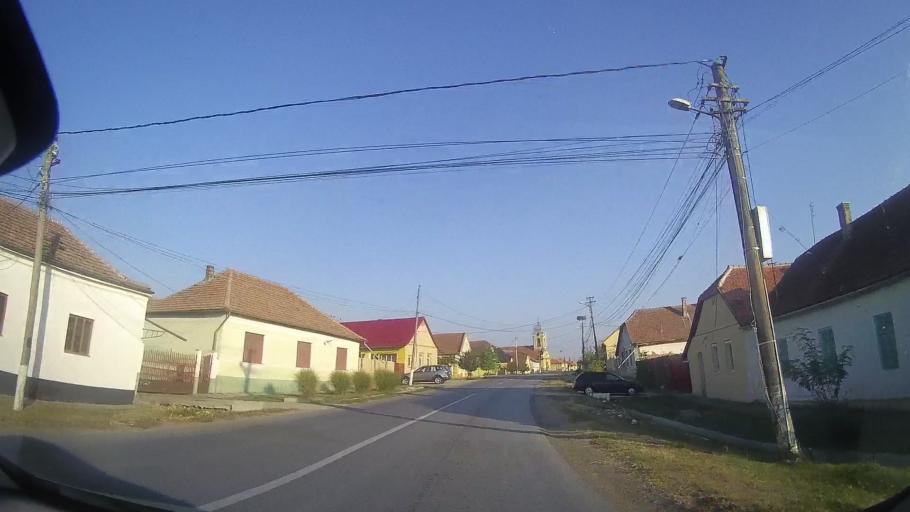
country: RO
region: Timis
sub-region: Comuna Pischia
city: Pischia
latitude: 45.9003
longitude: 21.3405
